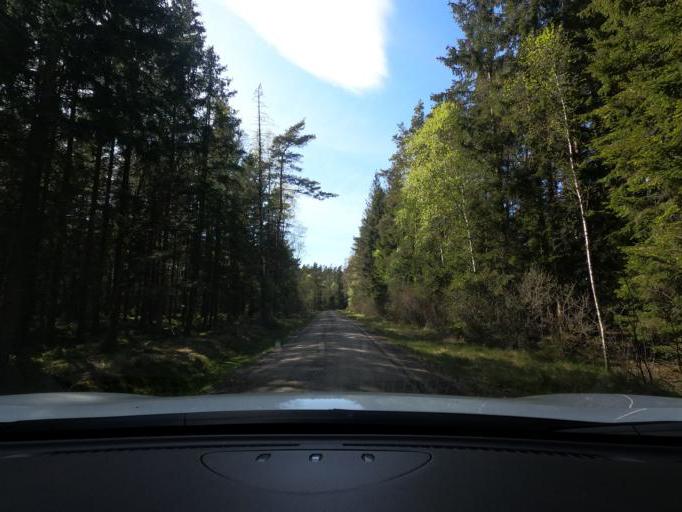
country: SE
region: Vaestra Goetaland
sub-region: Harryda Kommun
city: Ravlanda
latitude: 57.5943
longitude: 12.4805
